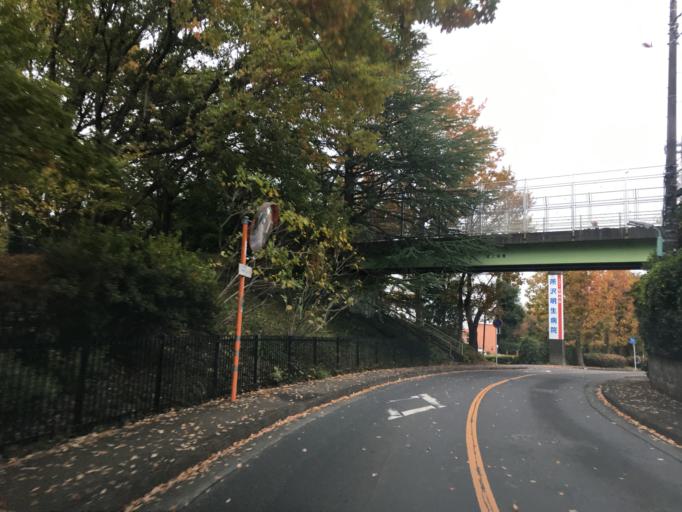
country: JP
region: Saitama
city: Tokorozawa
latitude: 35.7811
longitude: 139.4320
